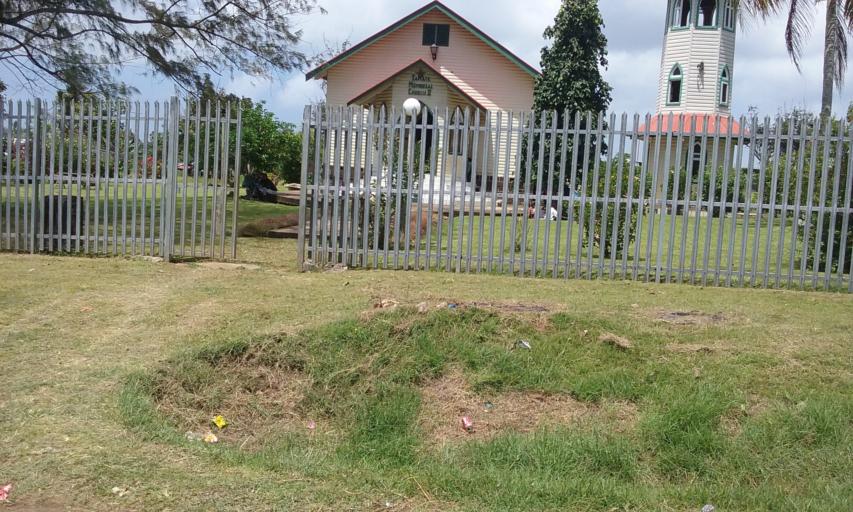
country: PG
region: Western Province
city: Daru
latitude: -9.0752
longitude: 143.2103
